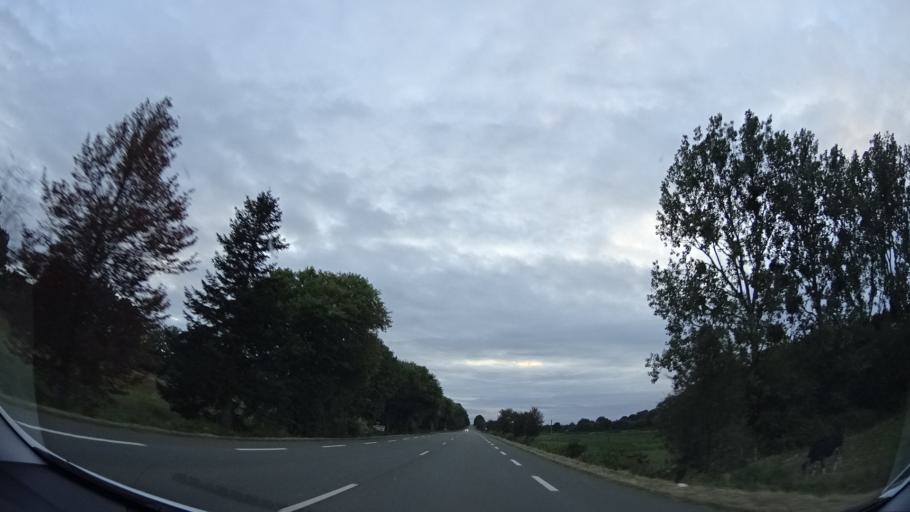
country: FR
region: Pays de la Loire
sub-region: Departement de la Mayenne
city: Vaiges
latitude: 48.0378
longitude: -0.4016
